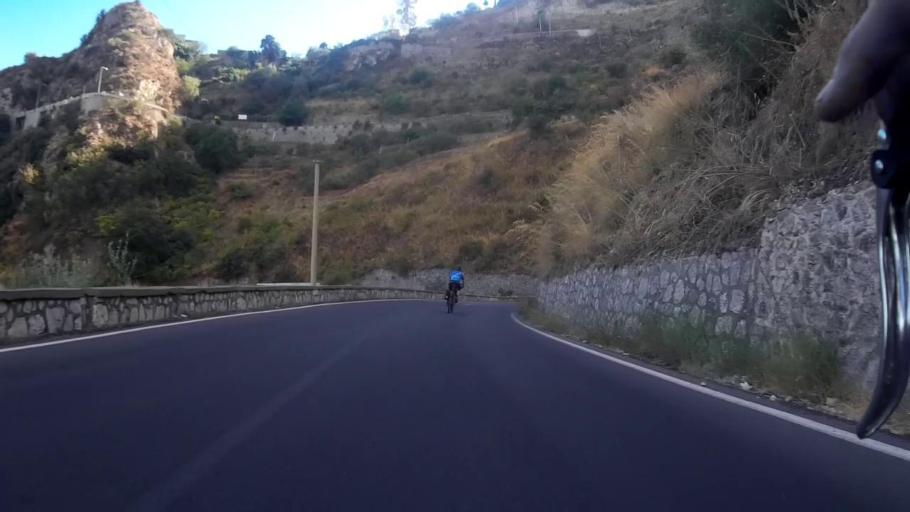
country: IT
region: Sicily
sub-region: Messina
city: Castelmola
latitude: 37.8638
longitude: 15.2770
